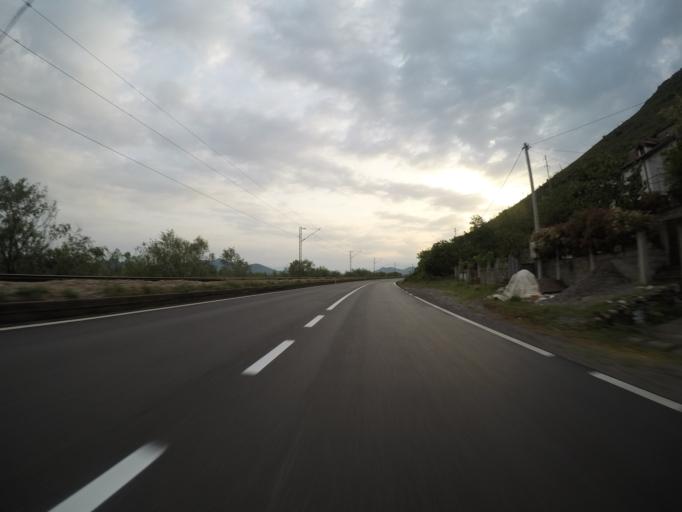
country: ME
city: Mojanovici
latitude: 42.2769
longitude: 19.1259
